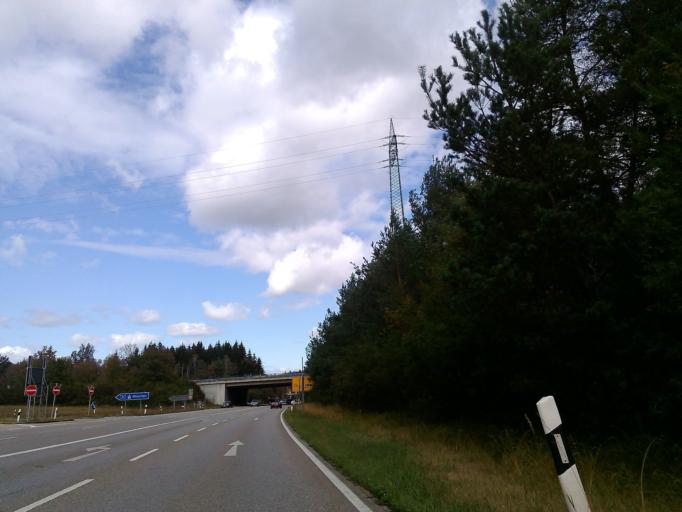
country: DE
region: Bavaria
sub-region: Upper Bavaria
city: Germering
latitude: 48.1157
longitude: 11.3845
